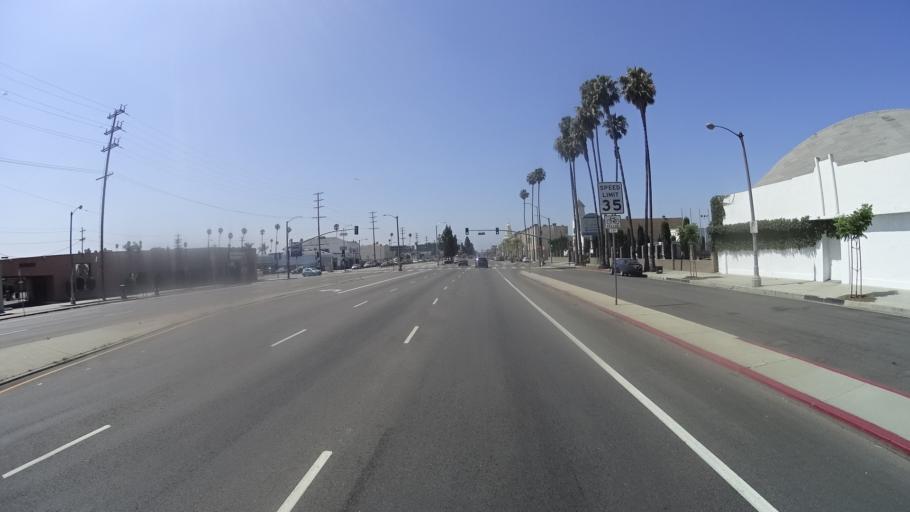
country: US
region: California
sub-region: Los Angeles County
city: Westmont
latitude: 33.9686
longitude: -118.2918
